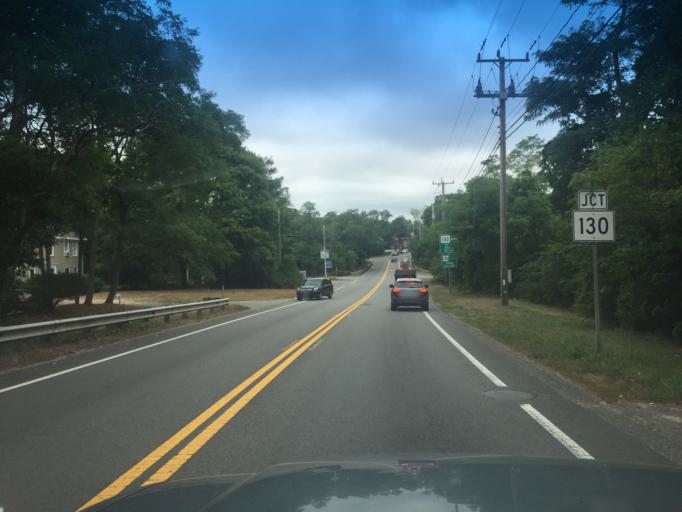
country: US
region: Massachusetts
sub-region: Barnstable County
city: Cotuit
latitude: 41.6366
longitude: -70.4539
